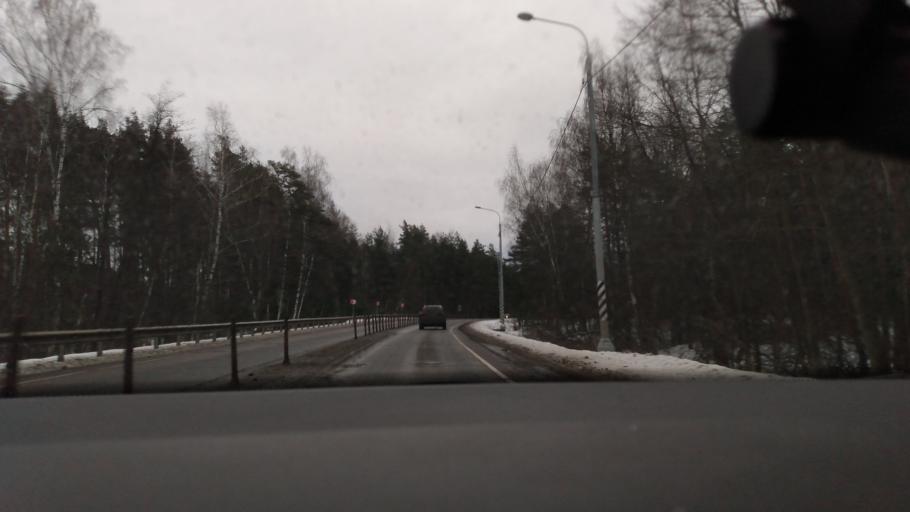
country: RU
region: Moskovskaya
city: Il'inskiy Pogost
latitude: 55.4994
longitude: 38.8170
